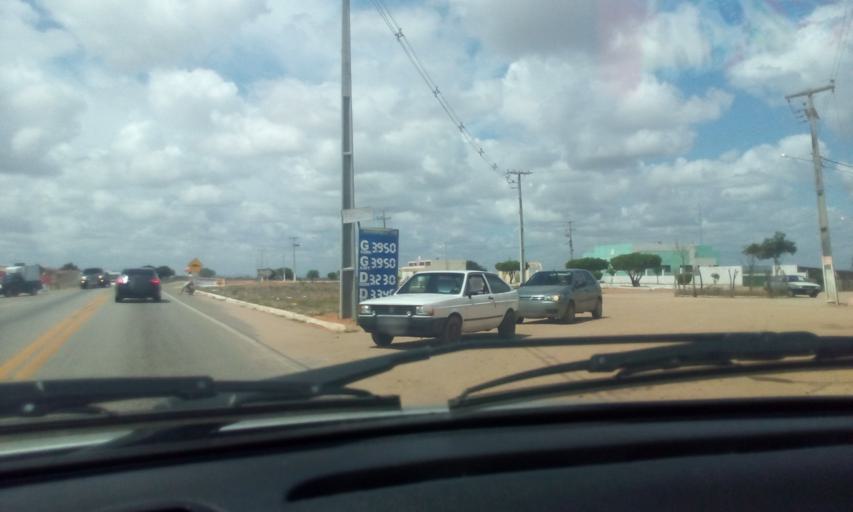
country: BR
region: Rio Grande do Norte
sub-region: Sao Paulo Do Potengi
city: Sao Paulo do Potengi
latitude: -5.9868
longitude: -35.5872
